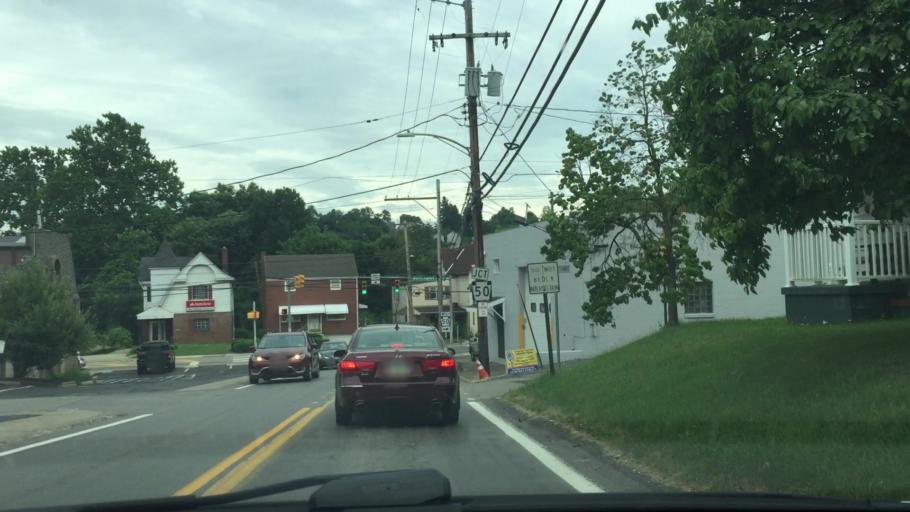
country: US
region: Pennsylvania
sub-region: Allegheny County
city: Bridgeville
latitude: 40.3628
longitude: -80.1112
